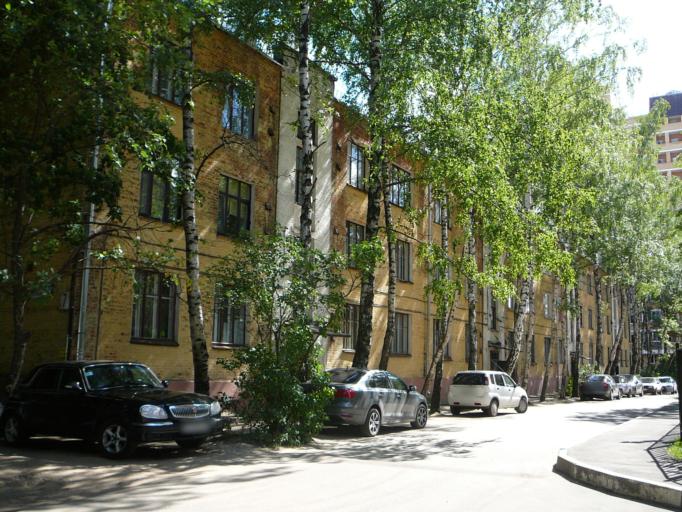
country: RU
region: Moskovskaya
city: Krasnogorsk
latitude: 55.8330
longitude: 37.3279
